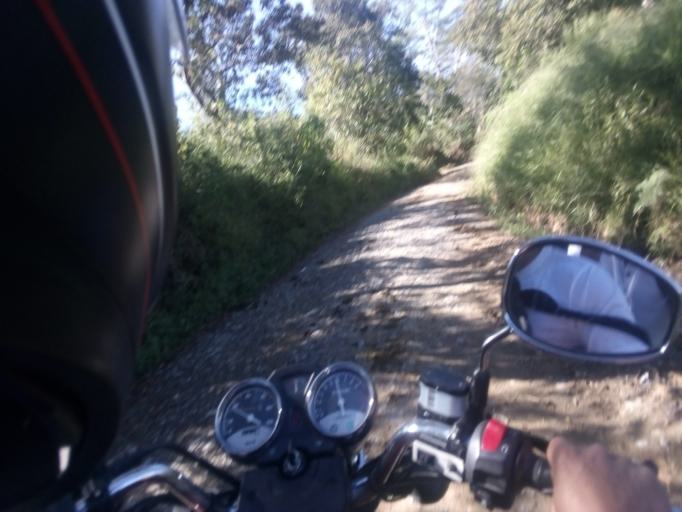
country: CO
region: Santander
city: Guepsa
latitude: 5.9957
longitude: -73.5546
